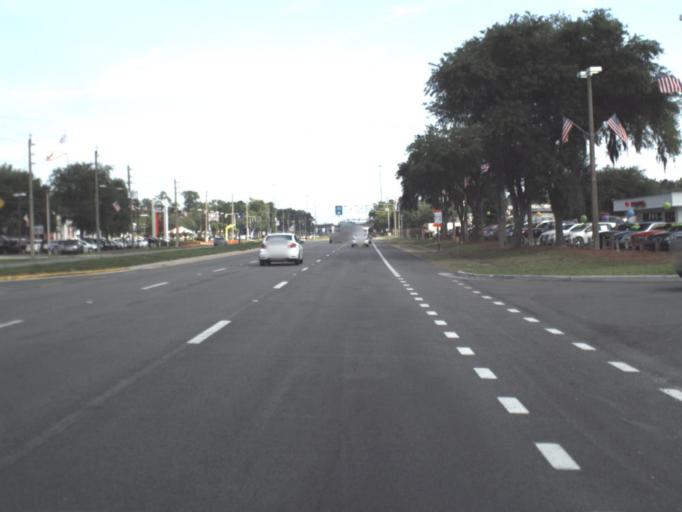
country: US
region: Florida
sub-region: Saint Johns County
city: Fruit Cove
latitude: 30.1734
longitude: -81.5469
